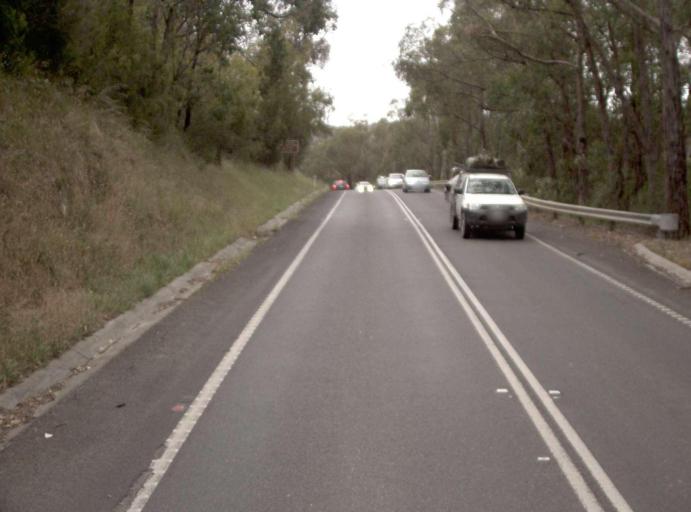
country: AU
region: Victoria
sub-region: Yarra Ranges
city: Yarra Glen
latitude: -37.5630
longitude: 145.4161
